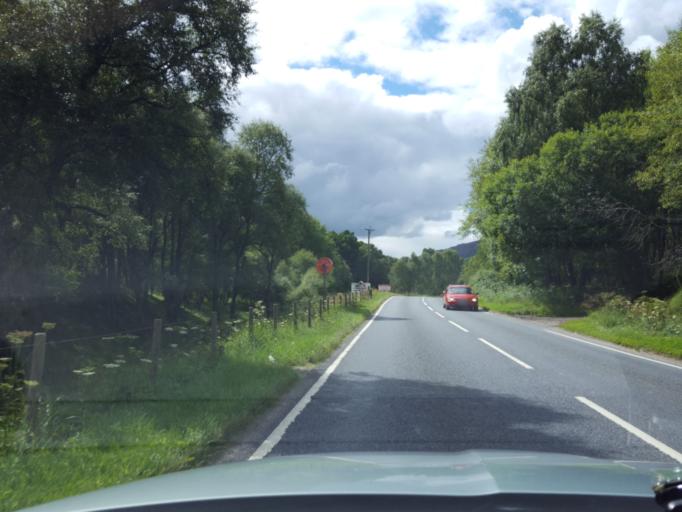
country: GB
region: Scotland
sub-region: Highland
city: Aviemore
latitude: 57.2127
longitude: -3.8216
